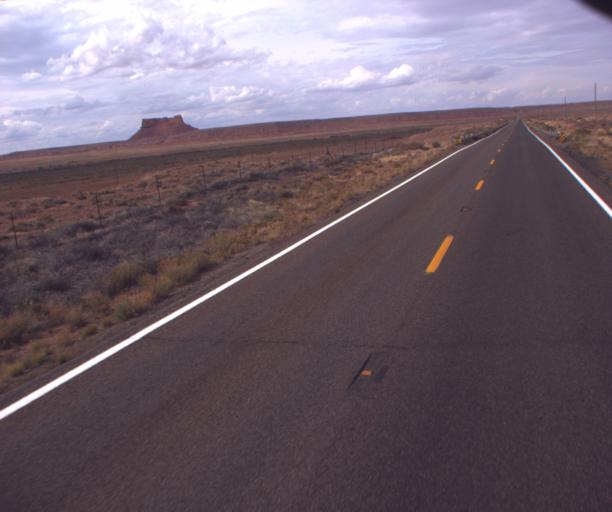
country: US
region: Arizona
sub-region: Apache County
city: Many Farms
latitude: 36.5215
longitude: -109.4924
